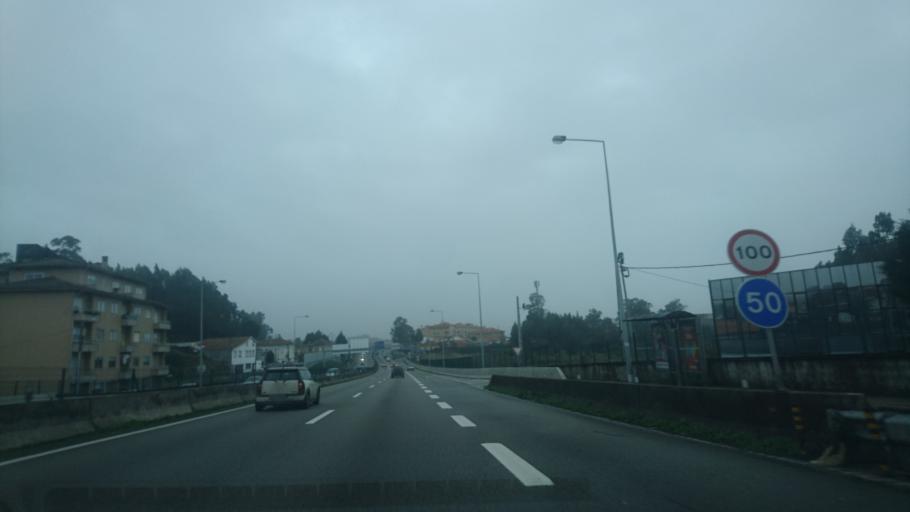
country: PT
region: Porto
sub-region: Vila Nova de Gaia
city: Vilar do Paraiso
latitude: 41.1055
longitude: -8.6265
